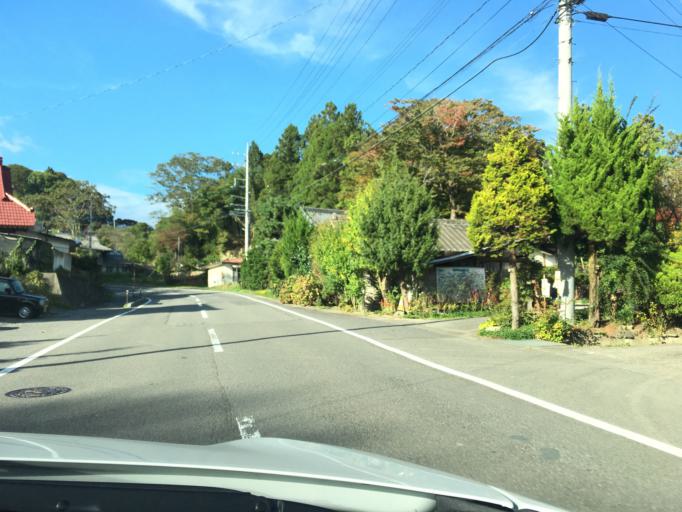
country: JP
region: Fukushima
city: Ishikawa
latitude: 37.2030
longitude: 140.4563
